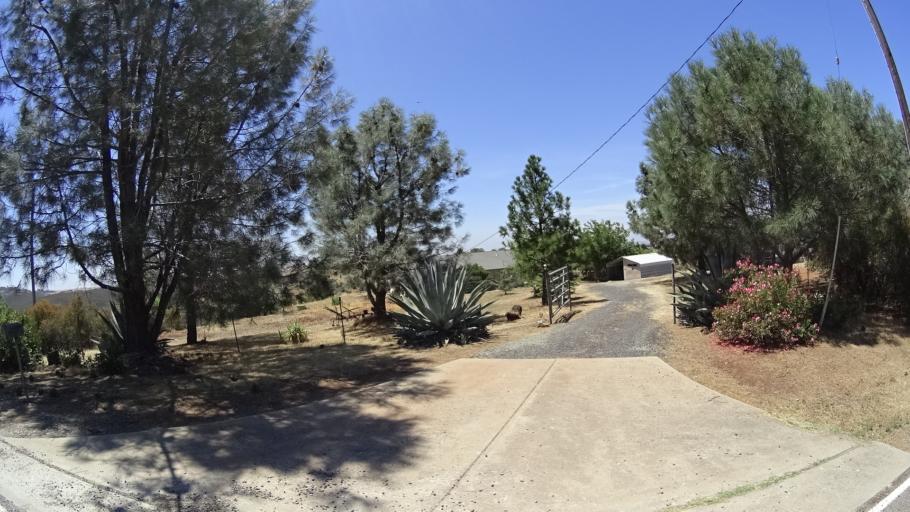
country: US
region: California
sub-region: Calaveras County
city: Rancho Calaveras
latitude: 38.1179
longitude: -120.8453
